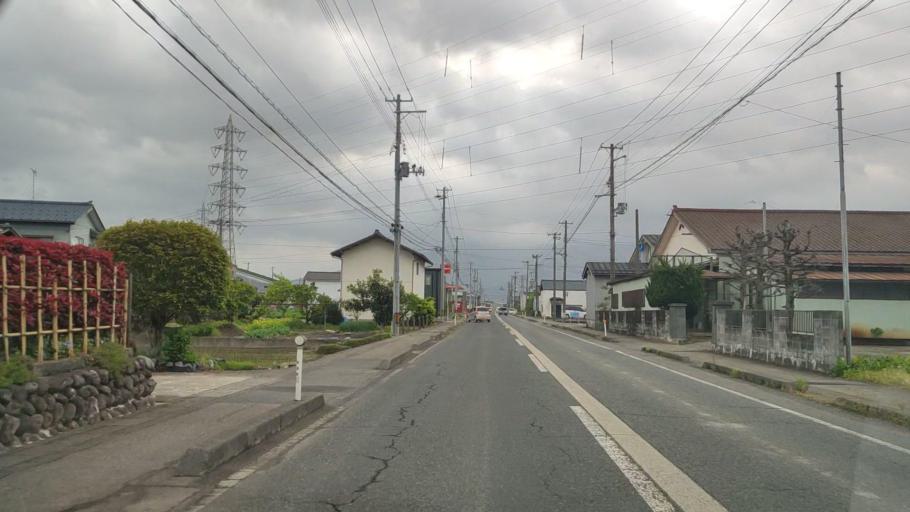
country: JP
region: Niigata
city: Gosen
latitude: 37.7342
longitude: 139.1959
